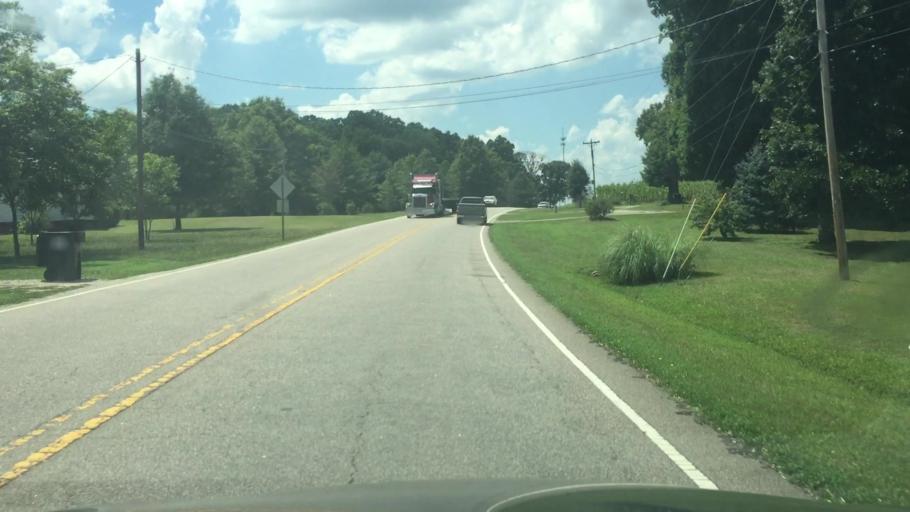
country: US
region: North Carolina
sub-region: Rowan County
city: Enochville
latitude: 35.5725
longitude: -80.6845
